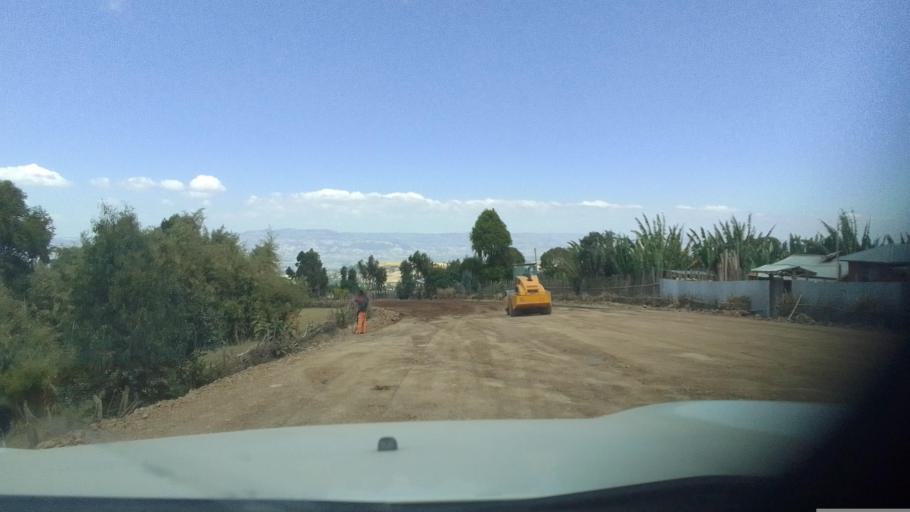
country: ET
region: Oromiya
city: Hagere Hiywet
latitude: 8.8521
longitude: 37.8930
